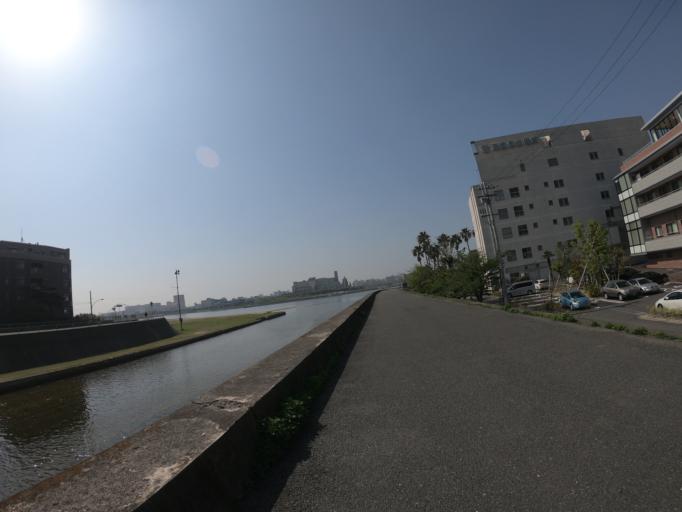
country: JP
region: Hyogo
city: Nishinomiya-hama
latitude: 34.7258
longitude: 135.3286
